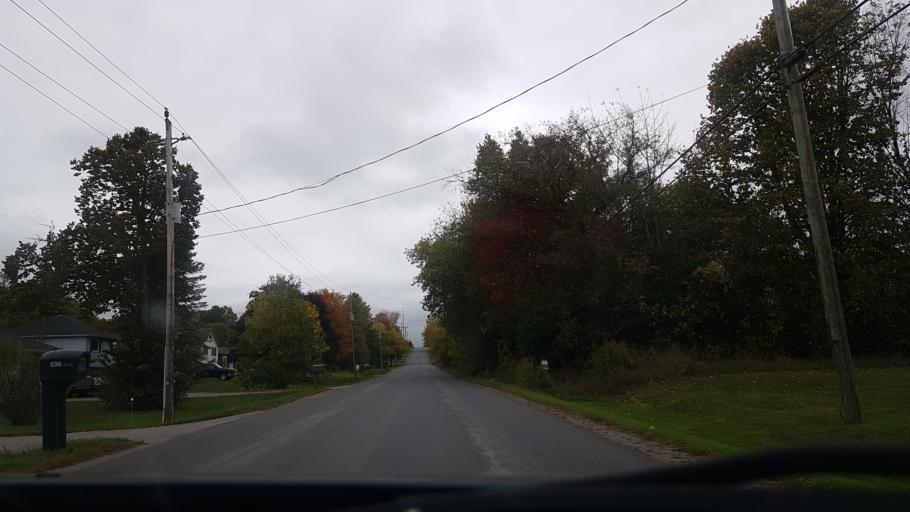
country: CA
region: Ontario
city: Omemee
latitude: 44.2470
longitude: -78.4380
